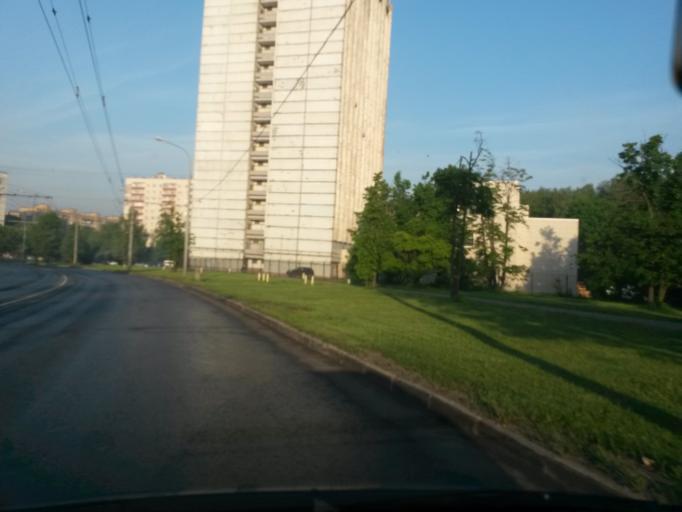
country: RU
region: Moscow
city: Gol'yanovo
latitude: 55.8226
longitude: 37.8003
